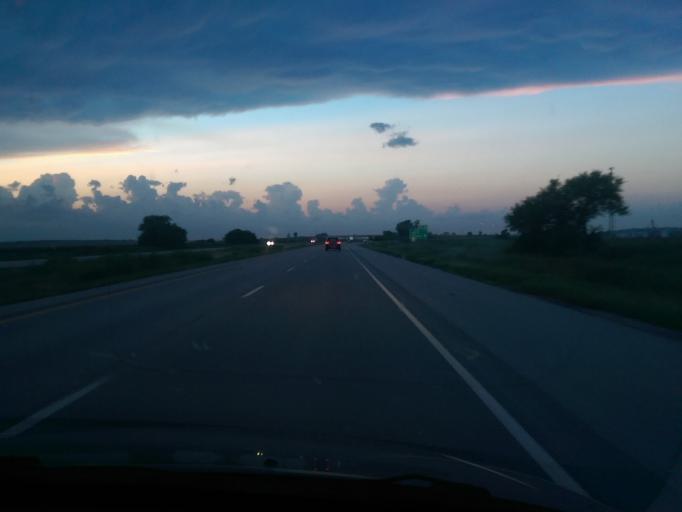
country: US
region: Nebraska
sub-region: Otoe County
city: Nebraska City
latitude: 40.7510
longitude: -95.8175
